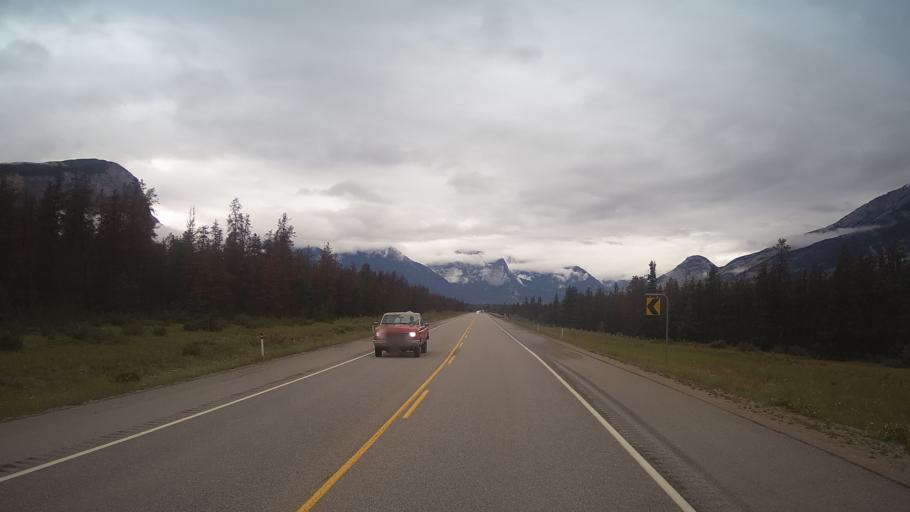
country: CA
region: Alberta
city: Jasper Park Lodge
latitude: 52.9497
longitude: -118.0405
